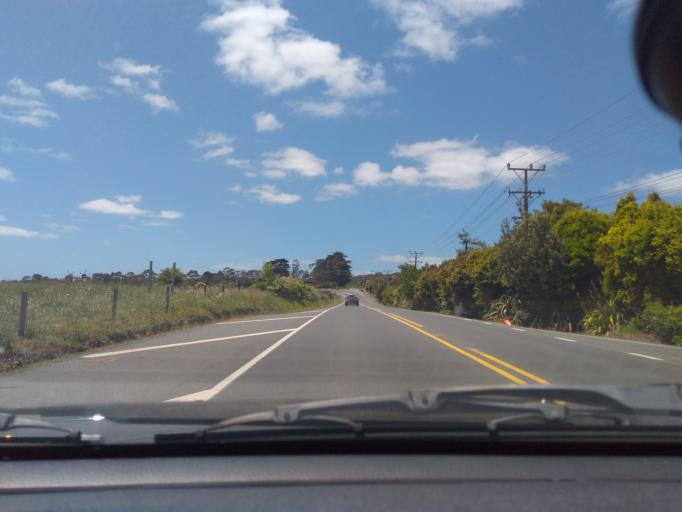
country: NZ
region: Auckland
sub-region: Auckland
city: Pakuranga
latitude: -36.9389
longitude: 174.9845
